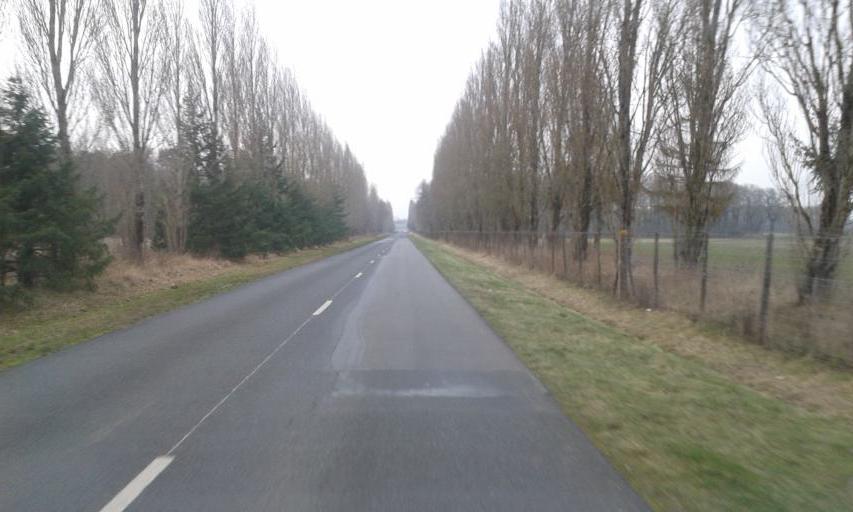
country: FR
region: Centre
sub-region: Departement du Loir-et-Cher
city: Saint-Laurent-Nouan
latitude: 47.6982
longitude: 1.6661
